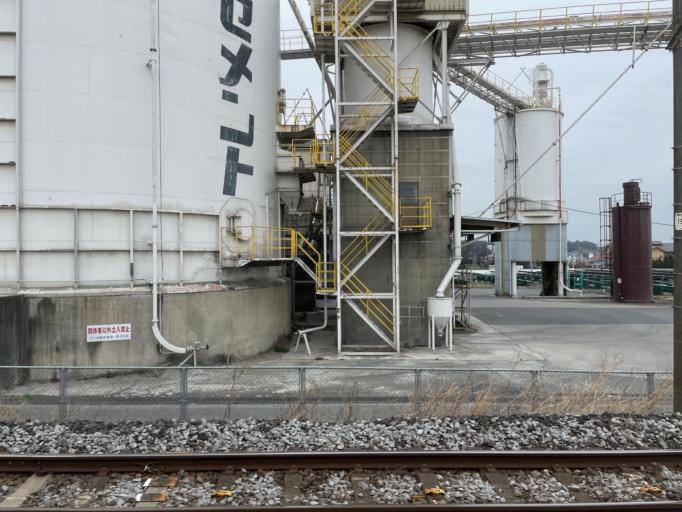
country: JP
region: Gunma
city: Shibukawa
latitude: 36.4673
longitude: 139.0186
